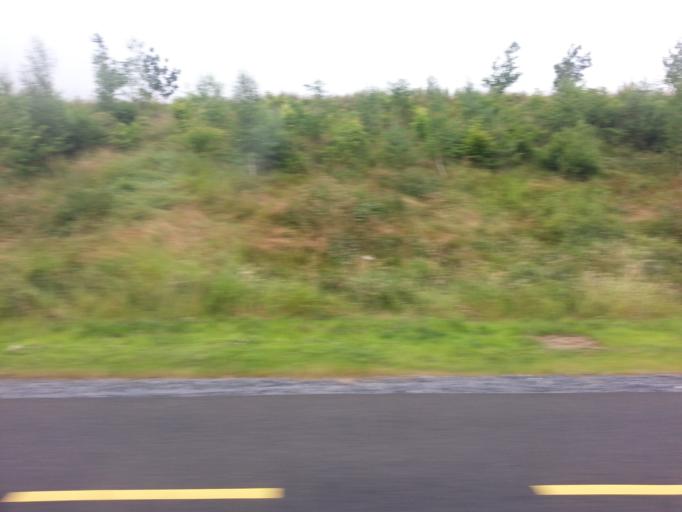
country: IE
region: Leinster
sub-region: Kilkenny
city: Kilkenny
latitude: 52.6446
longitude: -7.1840
